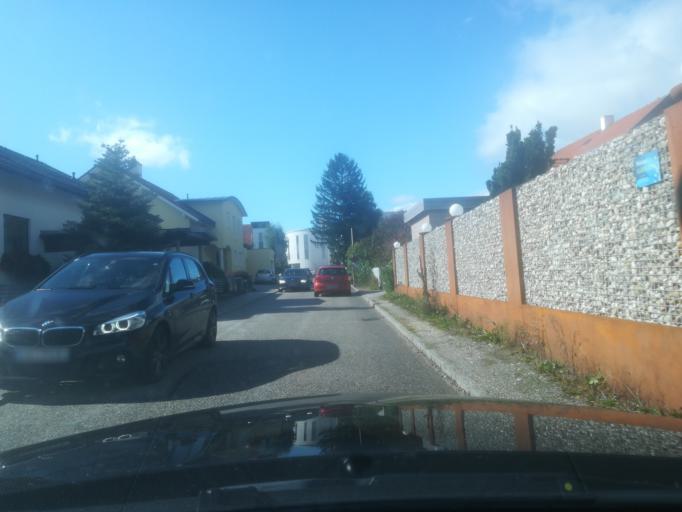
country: AT
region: Upper Austria
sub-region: Politischer Bezirk Urfahr-Umgebung
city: Eidenberg
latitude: 48.3588
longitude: 14.2596
